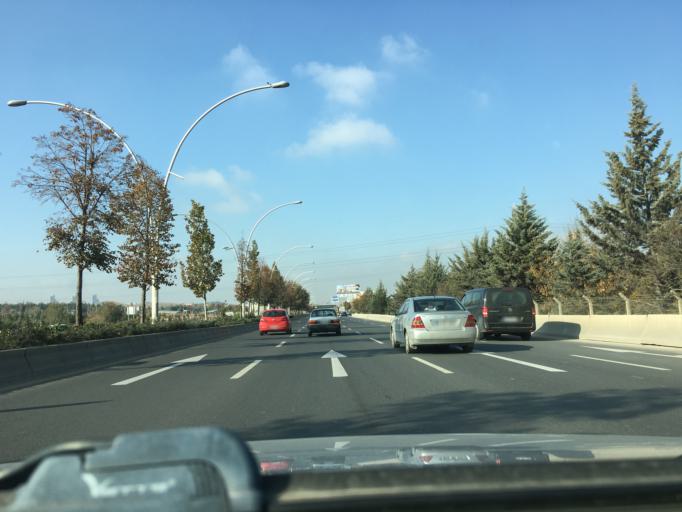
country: TR
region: Ankara
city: Batikent
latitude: 39.9068
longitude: 32.7380
